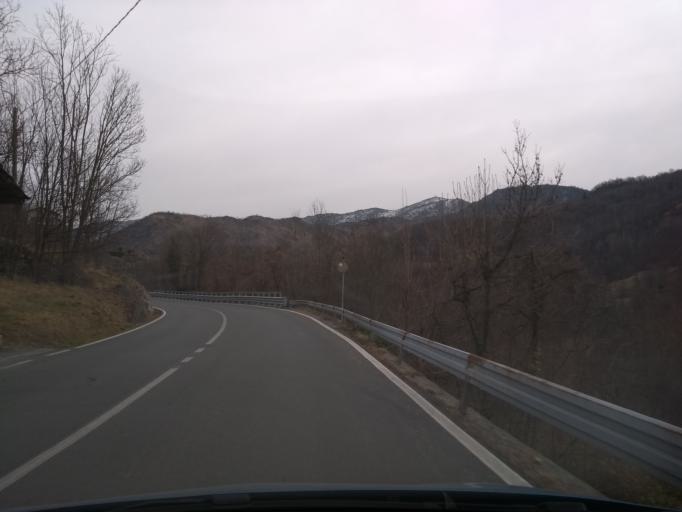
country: IT
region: Piedmont
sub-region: Provincia di Torino
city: Viu
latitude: 45.2370
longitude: 7.3931
